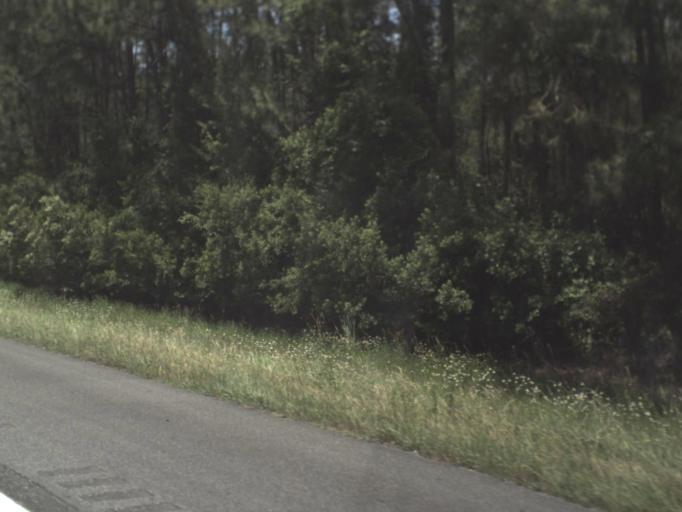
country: US
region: Florida
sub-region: Duval County
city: Baldwin
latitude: 30.2826
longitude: -82.0440
